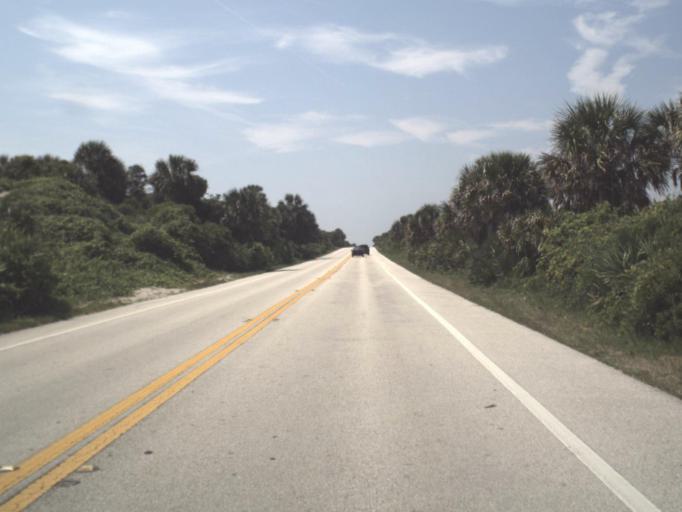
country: US
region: Florida
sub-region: Saint Johns County
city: Palm Valley
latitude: 30.1270
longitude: -81.3484
